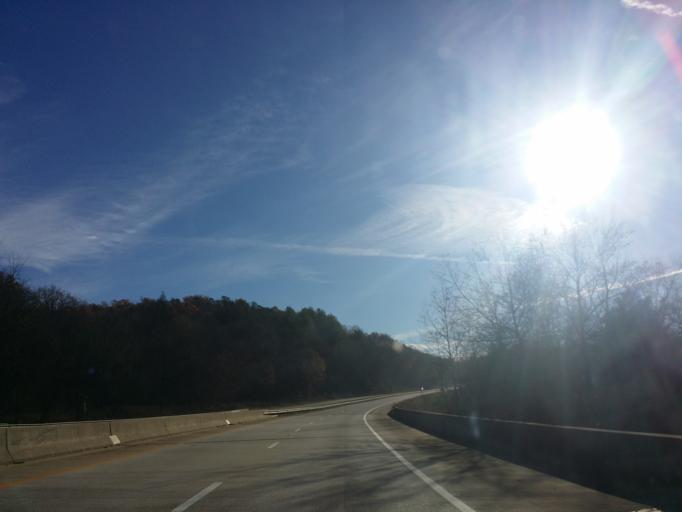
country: US
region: North Carolina
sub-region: McDowell County
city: West Marion
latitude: 35.6405
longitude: -82.1142
